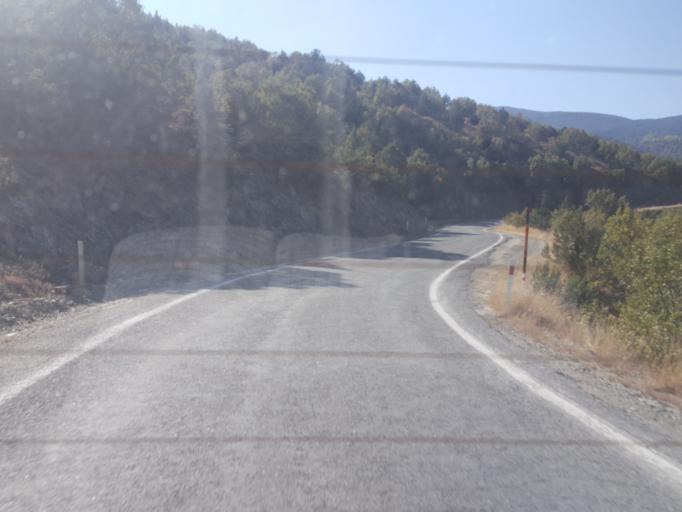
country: TR
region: Kastamonu
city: Tosya
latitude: 40.9922
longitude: 34.1753
